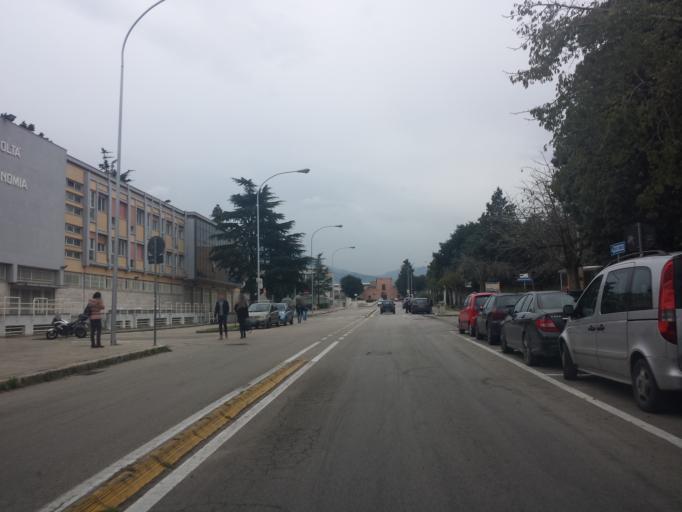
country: IT
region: Sicily
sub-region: Palermo
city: Palermo
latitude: 38.1035
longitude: 13.3484
